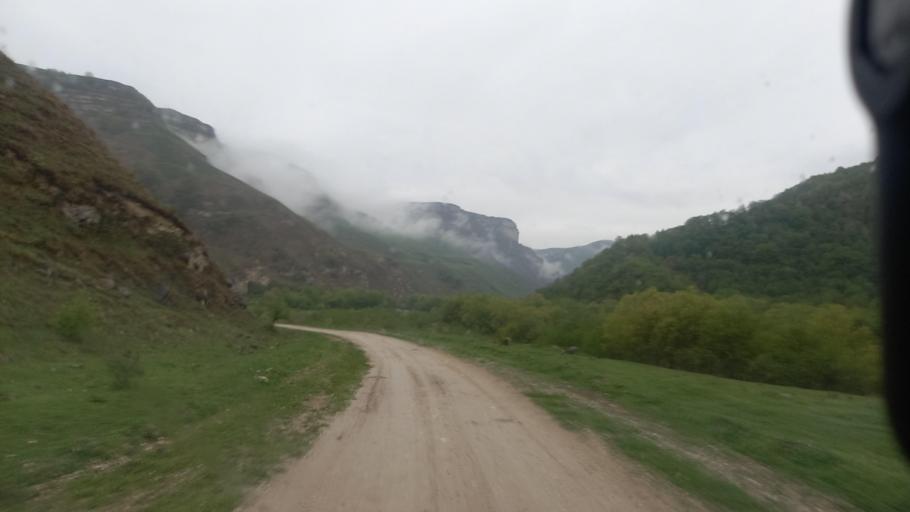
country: RU
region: Kabardino-Balkariya
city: Gundelen
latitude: 43.5969
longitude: 43.0655
